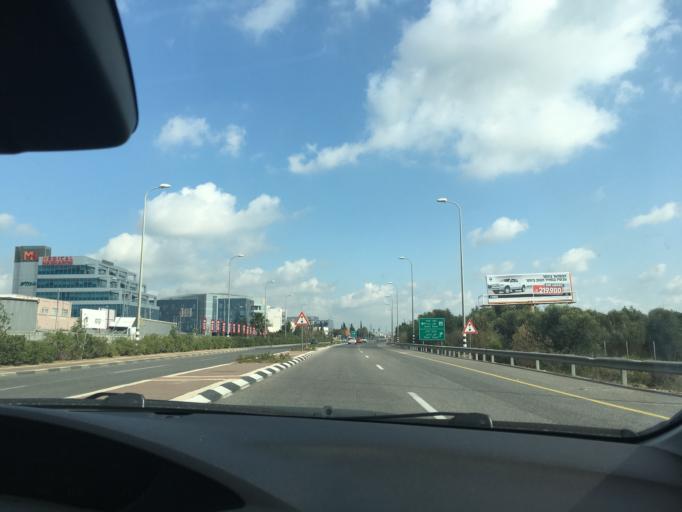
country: IL
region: Central District
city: Kfar Saba
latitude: 32.1739
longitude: 34.9329
